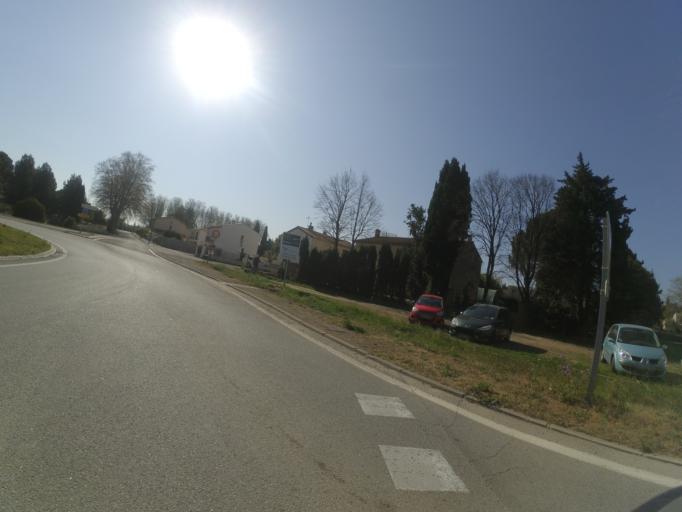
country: FR
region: Languedoc-Roussillon
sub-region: Departement des Pyrenees-Orientales
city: Thuir
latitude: 42.6370
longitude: 2.7498
